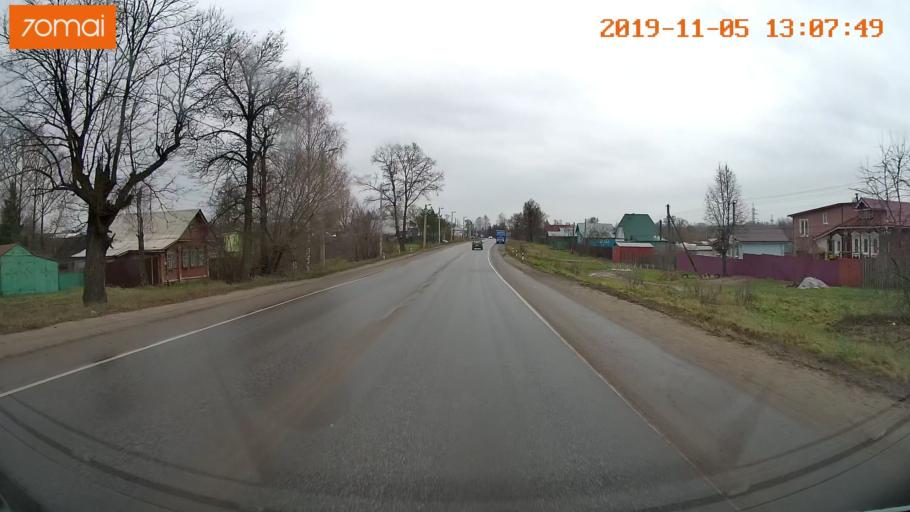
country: RU
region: Ivanovo
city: Kitovo
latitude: 56.8661
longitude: 41.2851
